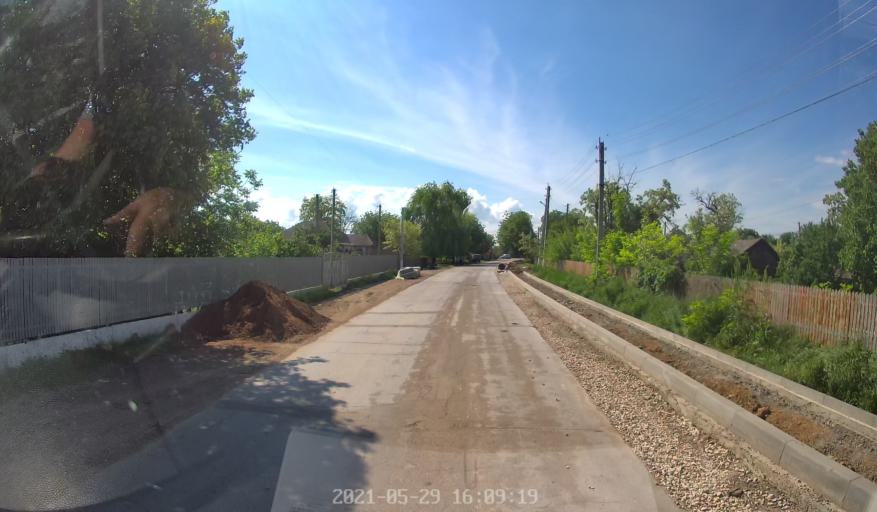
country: MD
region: Chisinau
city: Singera
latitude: 46.8201
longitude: 28.8830
